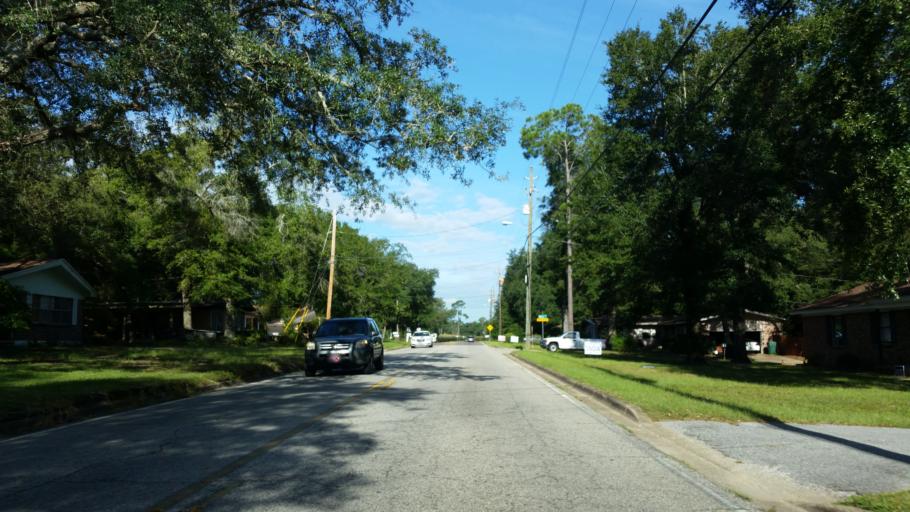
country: US
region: Florida
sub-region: Santa Rosa County
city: Milton
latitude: 30.6261
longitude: -87.0537
